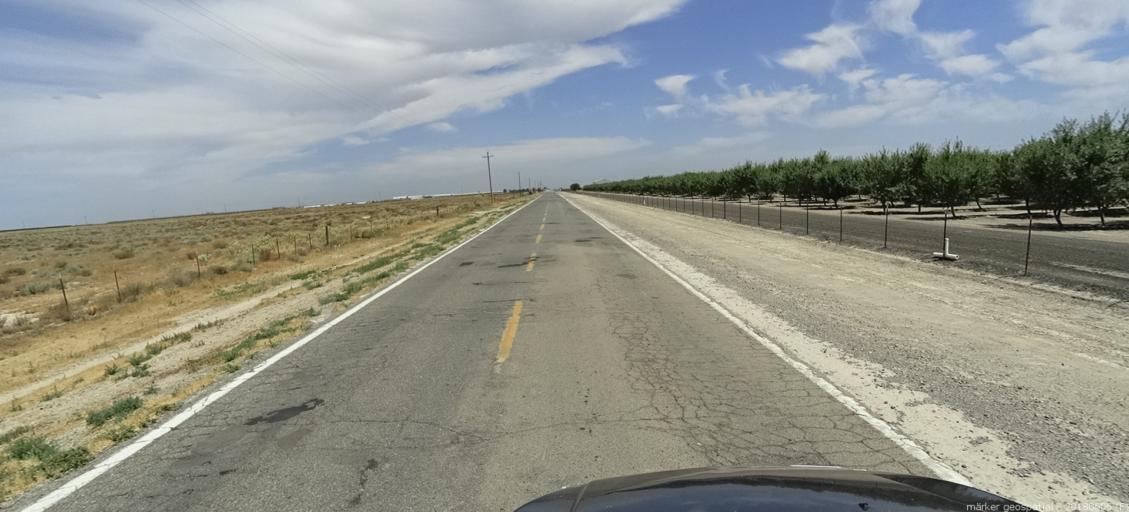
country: US
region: California
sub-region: Fresno County
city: Firebaugh
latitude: 36.9172
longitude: -120.3823
